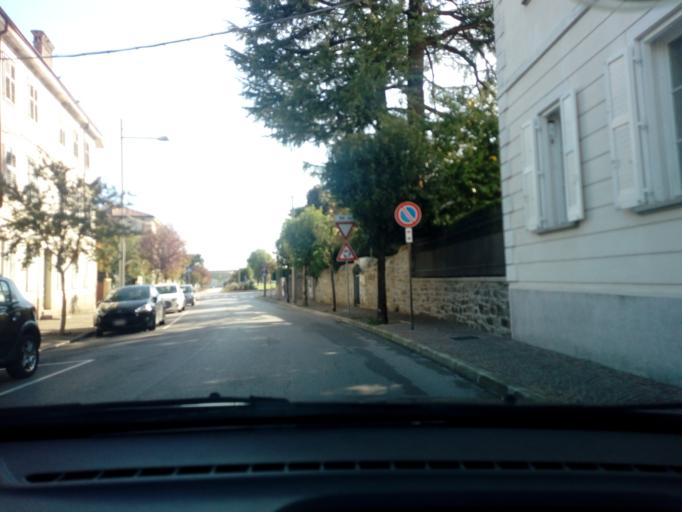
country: IT
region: Friuli Venezia Giulia
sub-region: Provincia di Gorizia
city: Cormons
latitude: 45.9570
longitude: 13.4717
